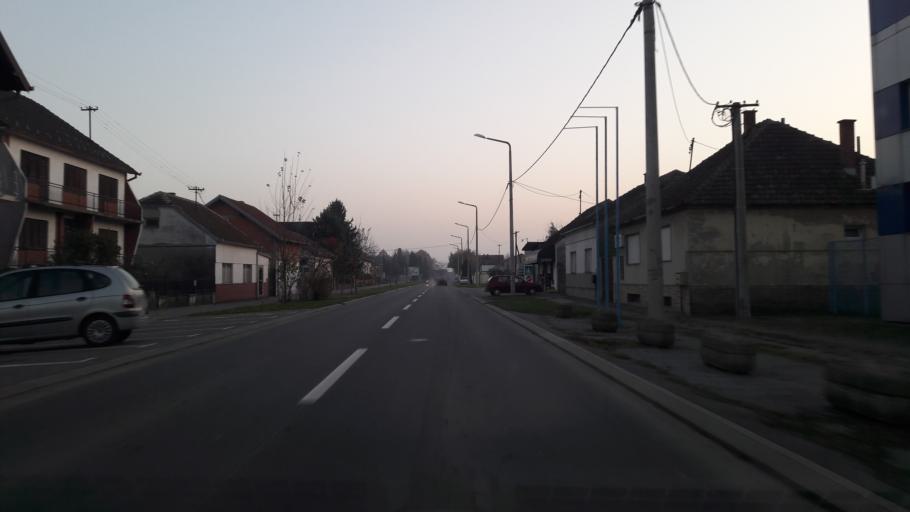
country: HR
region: Vukovarsko-Srijemska
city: Vukovar
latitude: 45.3342
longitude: 19.0023
